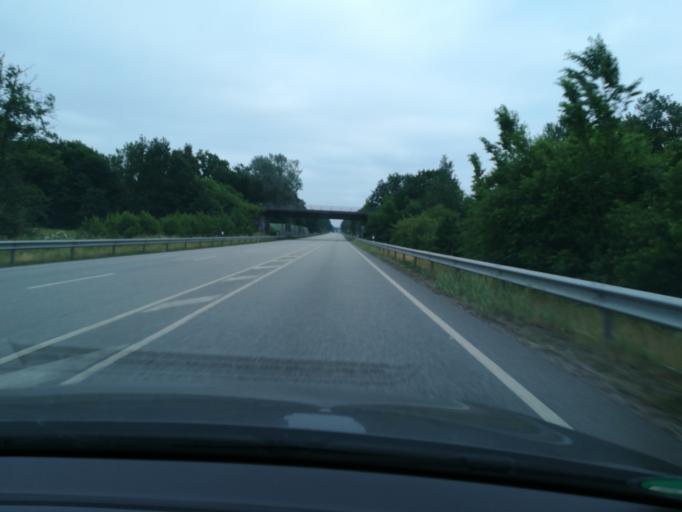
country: DE
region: Schleswig-Holstein
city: Grande
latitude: 53.6004
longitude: 10.3845
